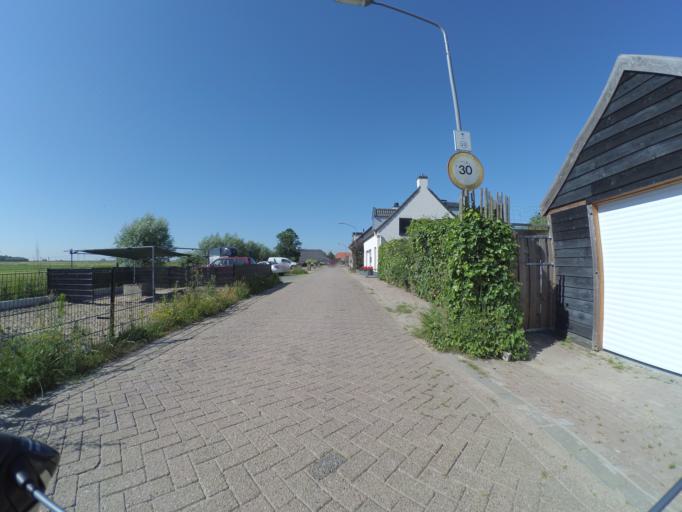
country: NL
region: North Brabant
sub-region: Gemeente Made en Drimmelen
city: Made
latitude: 51.6999
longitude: 4.7178
